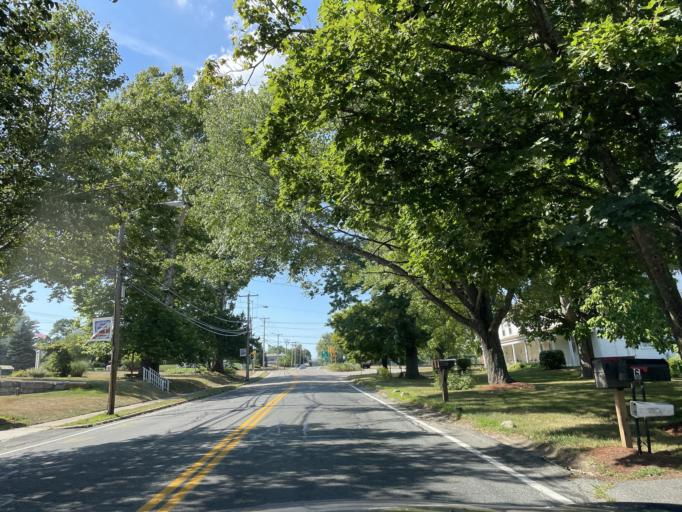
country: US
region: Massachusetts
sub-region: Worcester County
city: Mendon
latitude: 42.1068
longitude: -71.5528
